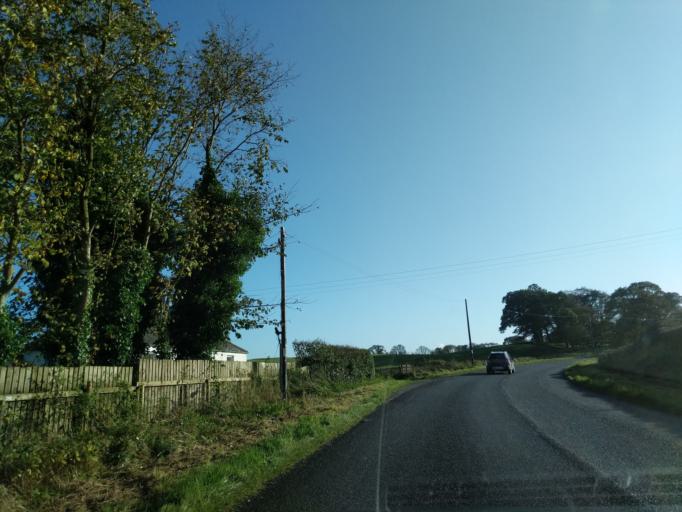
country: GB
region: Scotland
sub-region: Dumfries and Galloway
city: Kirkcudbright
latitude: 54.9077
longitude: -4.0062
